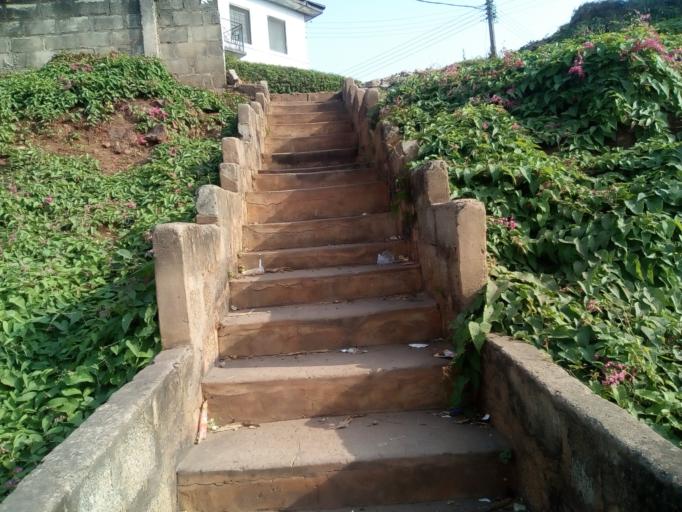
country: GH
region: Greater Accra
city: Accra
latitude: 5.5863
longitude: -0.2143
